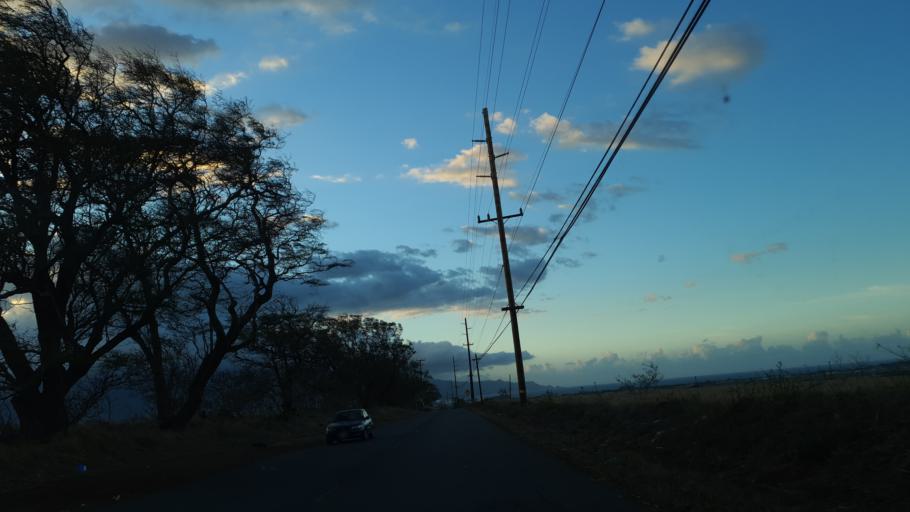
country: US
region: Hawaii
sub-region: Maui County
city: Kahului
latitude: 20.8632
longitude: -156.4294
